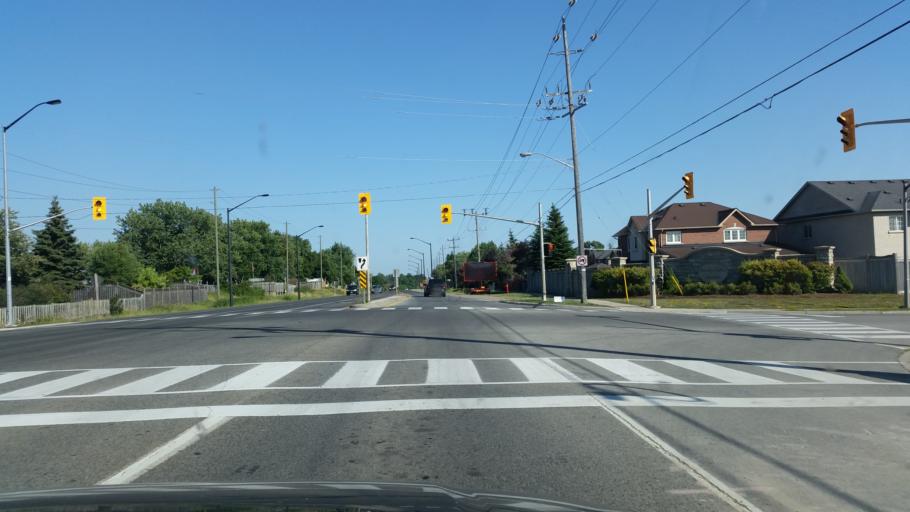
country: CA
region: Ontario
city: Brampton
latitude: 43.8876
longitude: -79.7494
